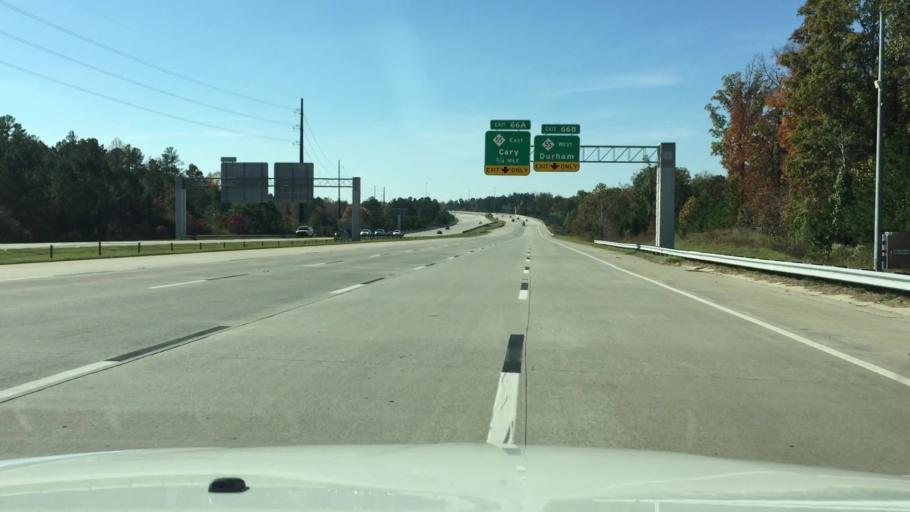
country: US
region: North Carolina
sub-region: Wake County
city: Morrisville
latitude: 35.8466
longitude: -78.8724
